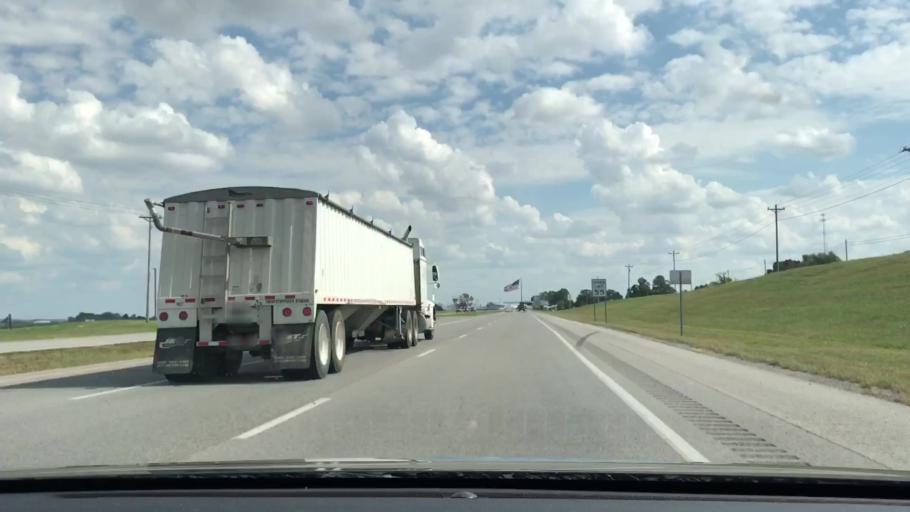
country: US
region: Kentucky
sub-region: Trigg County
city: Cadiz
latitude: 36.8765
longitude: -87.7492
